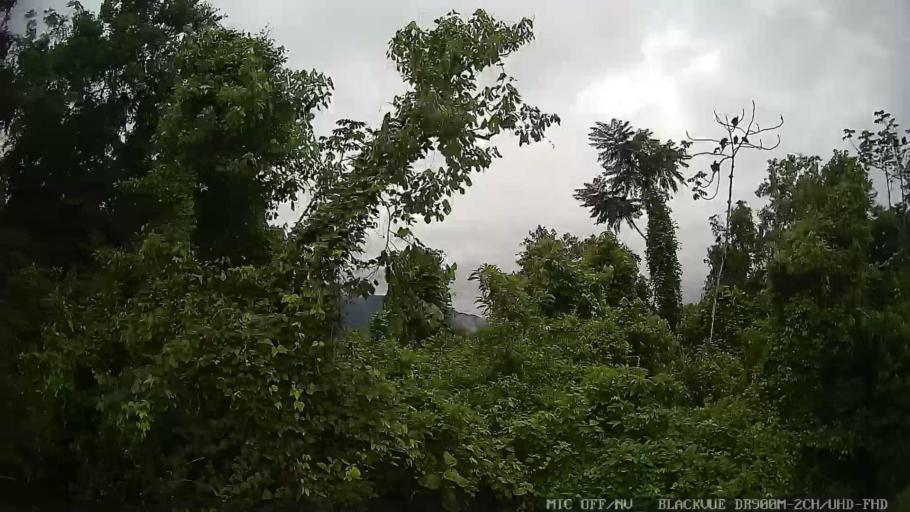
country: BR
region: Sao Paulo
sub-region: Sao Sebastiao
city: Sao Sebastiao
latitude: -23.7195
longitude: -45.4465
